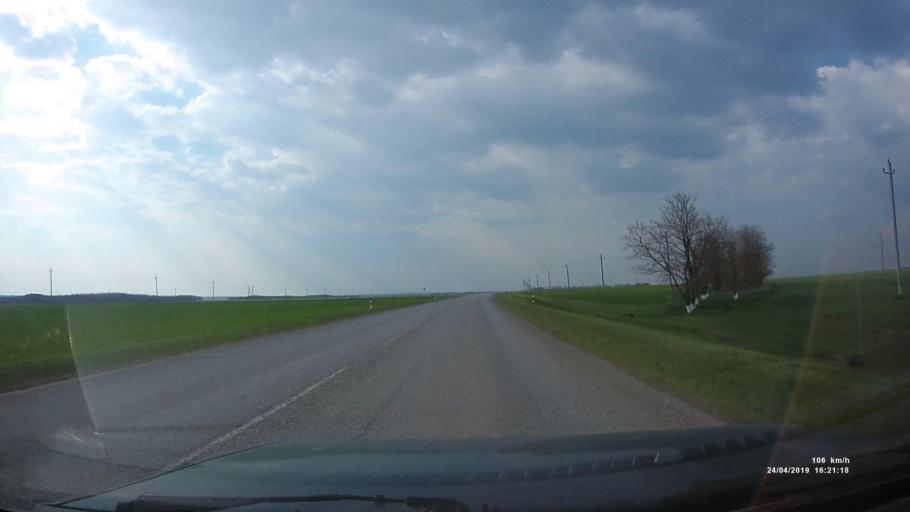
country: RU
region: Rostov
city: Orlovskiy
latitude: 46.8030
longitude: 42.0670
